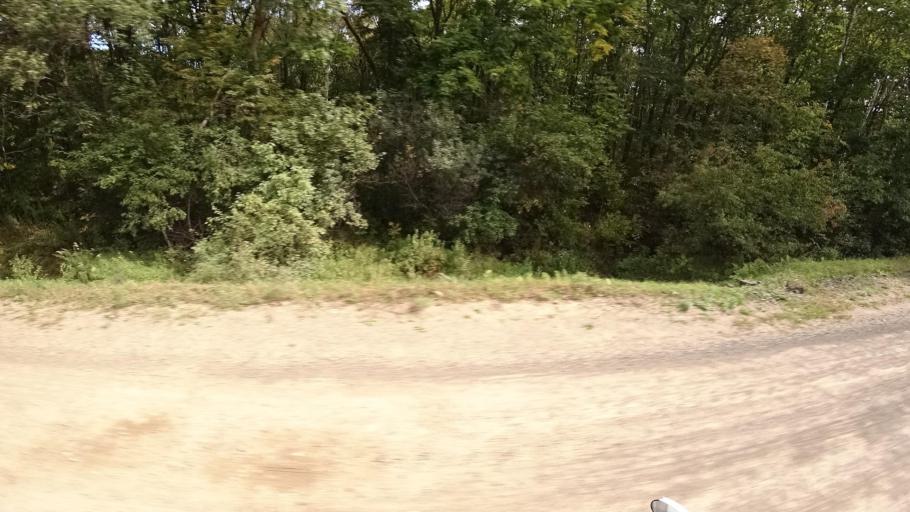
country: RU
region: Primorskiy
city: Yakovlevka
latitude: 44.7410
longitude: 133.6070
